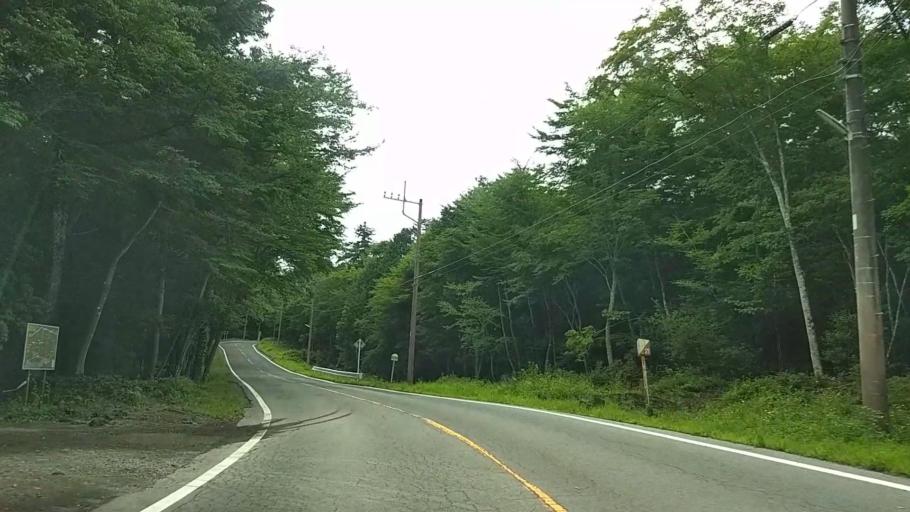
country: JP
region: Yamanashi
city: Fujikawaguchiko
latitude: 35.4871
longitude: 138.6672
